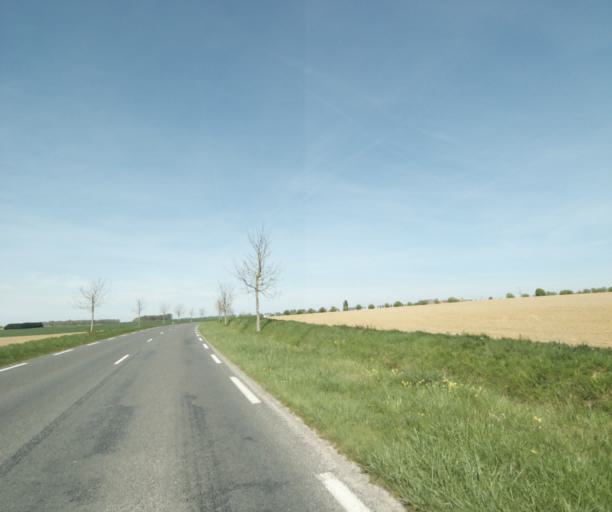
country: FR
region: Ile-de-France
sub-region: Departement de Seine-et-Marne
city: Nangis
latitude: 48.5525
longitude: 2.9983
